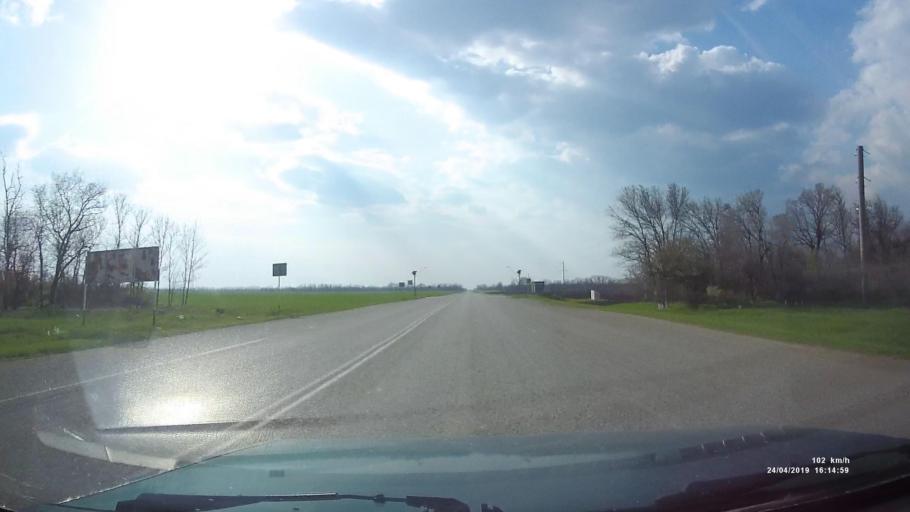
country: RU
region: Rostov
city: Sovetskoye
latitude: 46.7550
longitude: 42.1906
